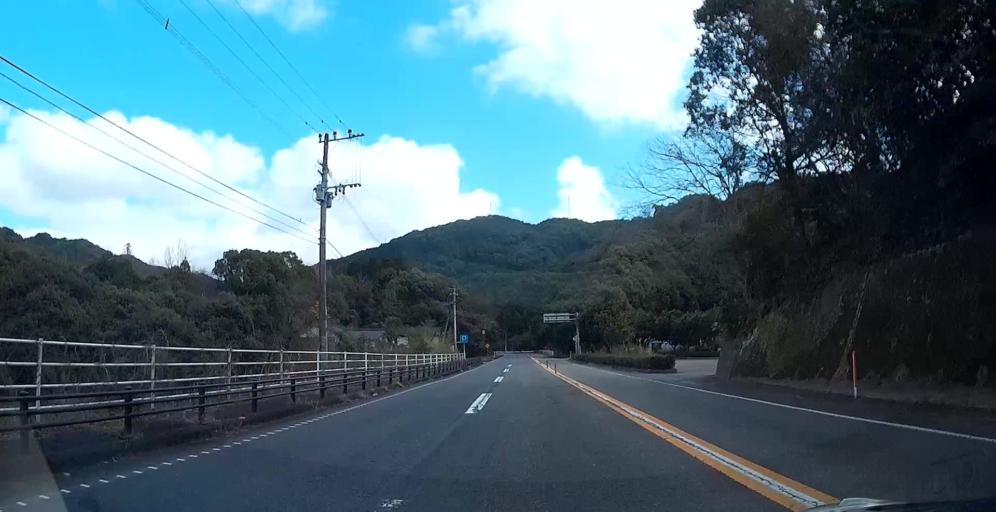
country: JP
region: Kumamoto
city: Yatsushiro
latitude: 32.3678
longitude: 130.5209
